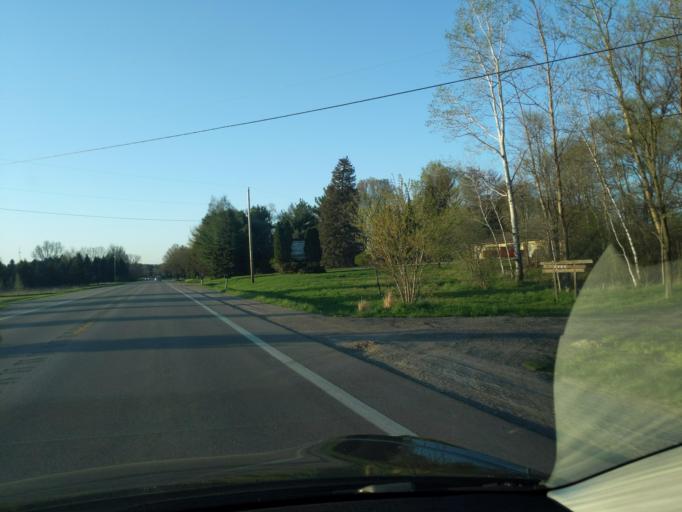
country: US
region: Michigan
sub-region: Ingham County
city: Stockbridge
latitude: 42.4306
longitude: -84.1726
